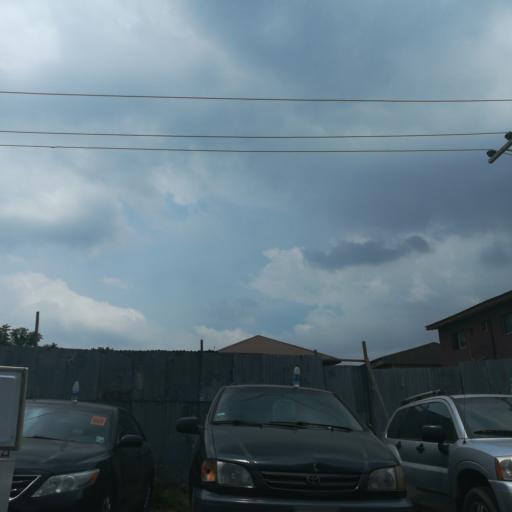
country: NG
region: Lagos
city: Ojota
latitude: 6.5832
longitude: 3.3843
